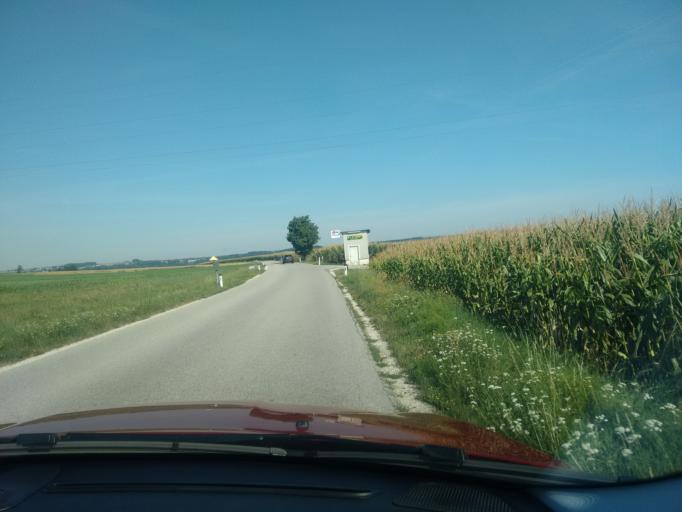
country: AT
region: Upper Austria
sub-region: Politischer Bezirk Steyr-Land
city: Pfarrkirchen bei Bad Hall
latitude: 48.0443
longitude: 14.1842
